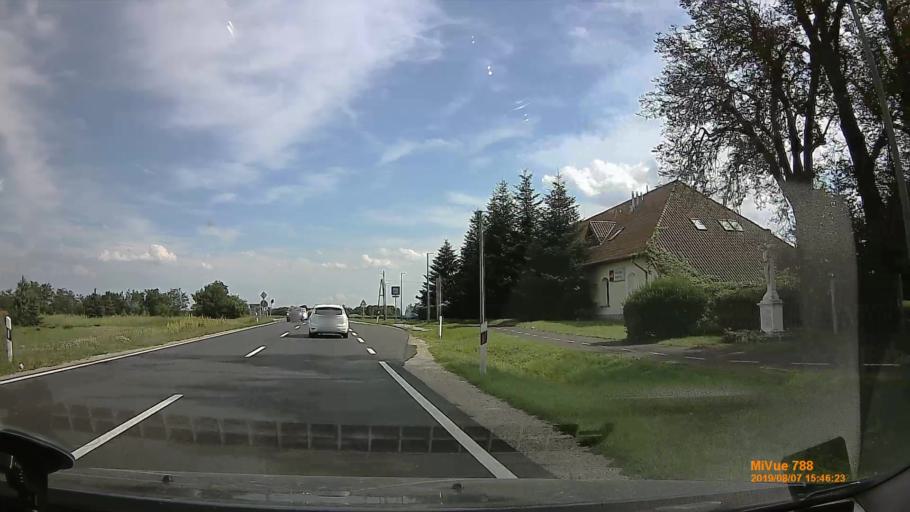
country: HU
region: Vas
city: Szombathely
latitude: 47.1856
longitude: 16.6208
